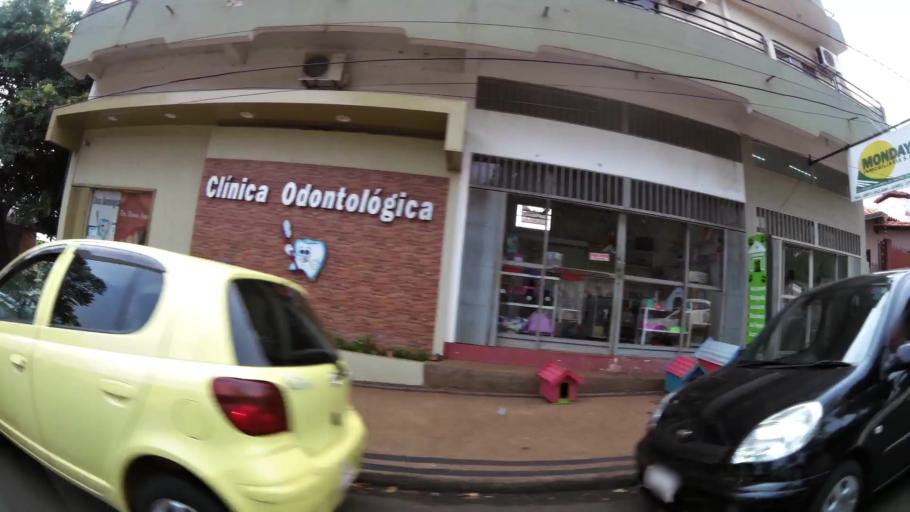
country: BR
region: Parana
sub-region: Foz Do Iguacu
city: Foz do Iguacu
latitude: -25.5563
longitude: -54.6055
